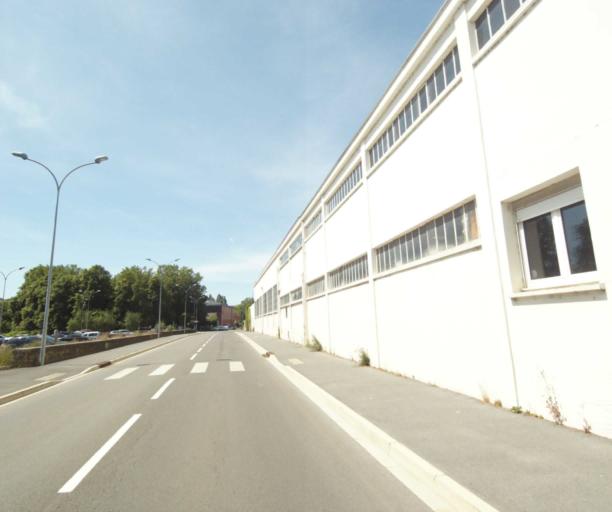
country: FR
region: Champagne-Ardenne
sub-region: Departement des Ardennes
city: Charleville-Mezieres
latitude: 49.7661
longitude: 4.7158
